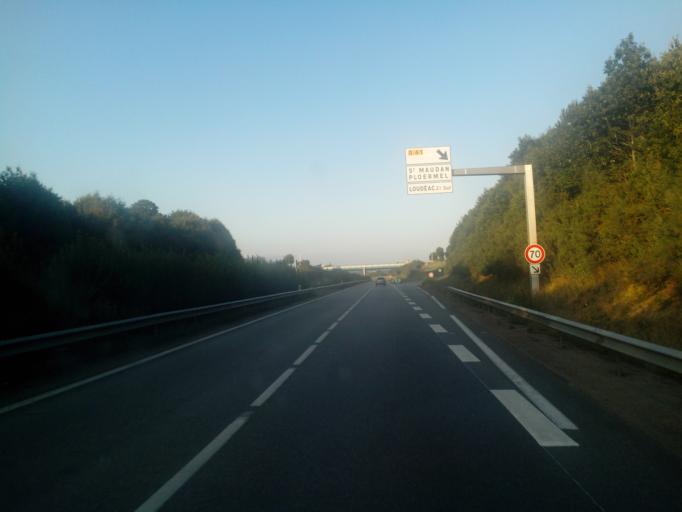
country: FR
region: Brittany
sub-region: Departement des Cotes-d'Armor
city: Loudeac
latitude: 48.1499
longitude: -2.7610
